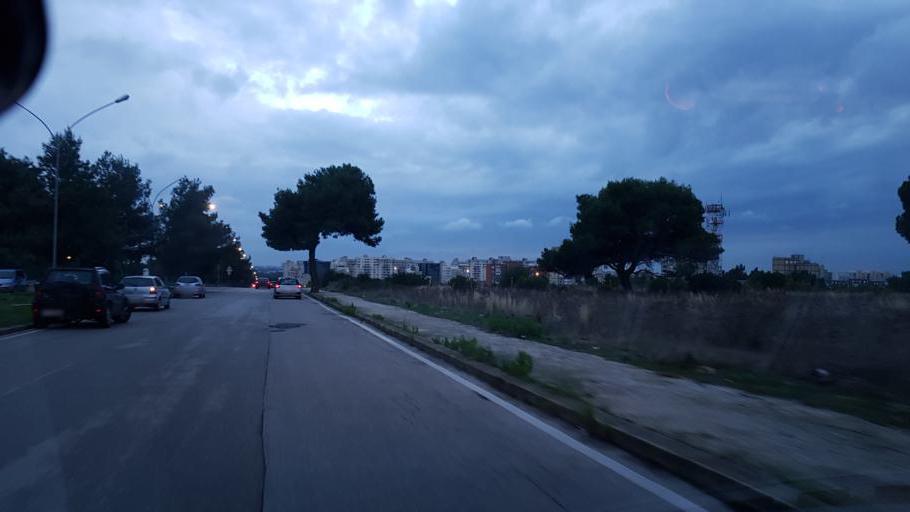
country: IT
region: Apulia
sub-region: Provincia di Taranto
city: Paolo VI
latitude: 40.5262
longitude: 17.2812
